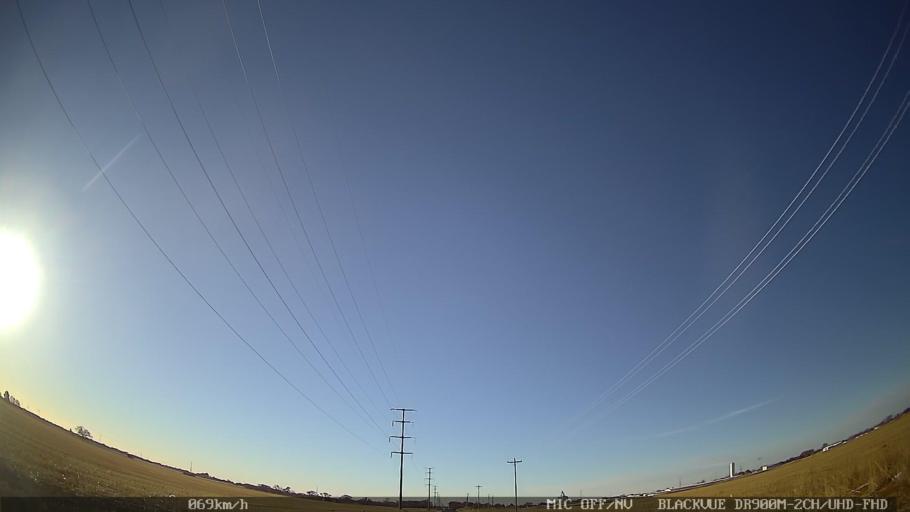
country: US
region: New Mexico
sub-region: Curry County
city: Clovis
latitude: 34.4210
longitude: -103.2493
